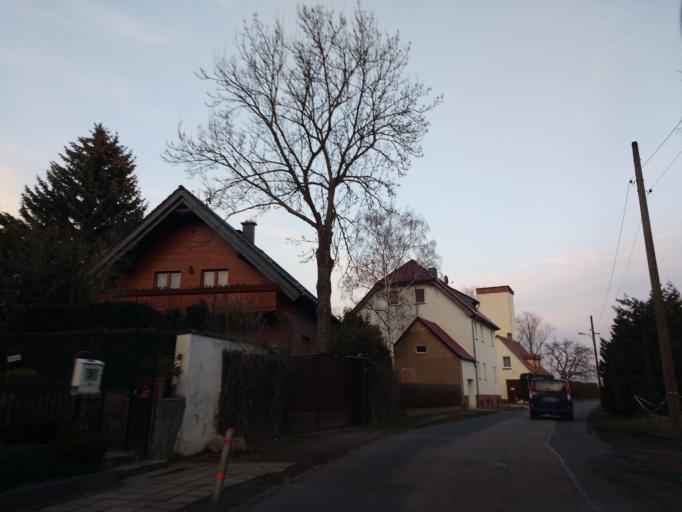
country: DE
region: Saxony-Anhalt
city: Halle (Saale)
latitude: 51.5151
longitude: 12.0115
